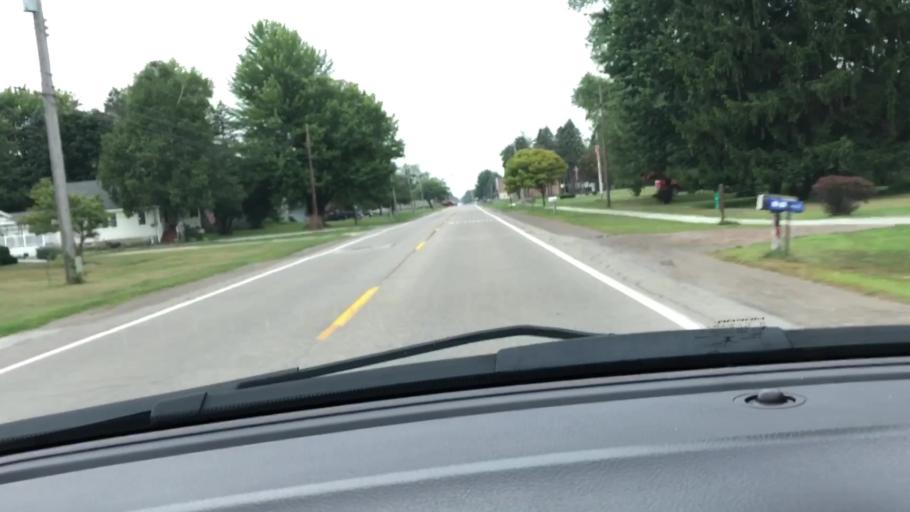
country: US
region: Michigan
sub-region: Bay County
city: Auburn
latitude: 43.6039
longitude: -84.1054
